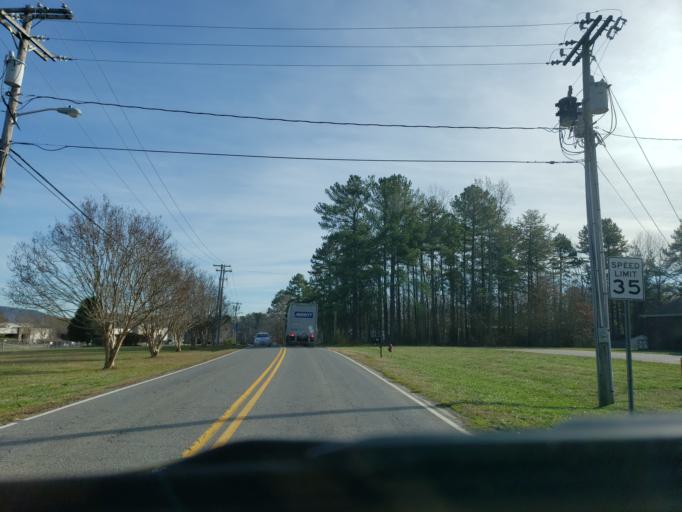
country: US
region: North Carolina
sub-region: Cleveland County
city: Kings Mountain
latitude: 35.2404
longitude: -81.3243
